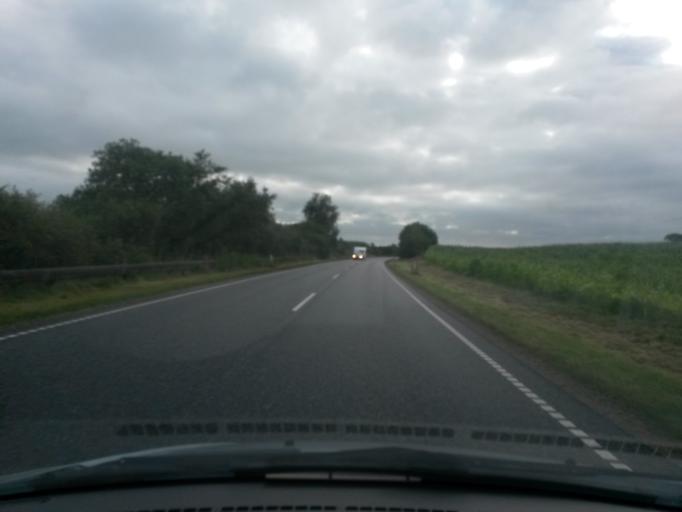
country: DK
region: Central Jutland
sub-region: Silkeborg Kommune
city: Kjellerup
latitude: 56.2996
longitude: 9.4139
